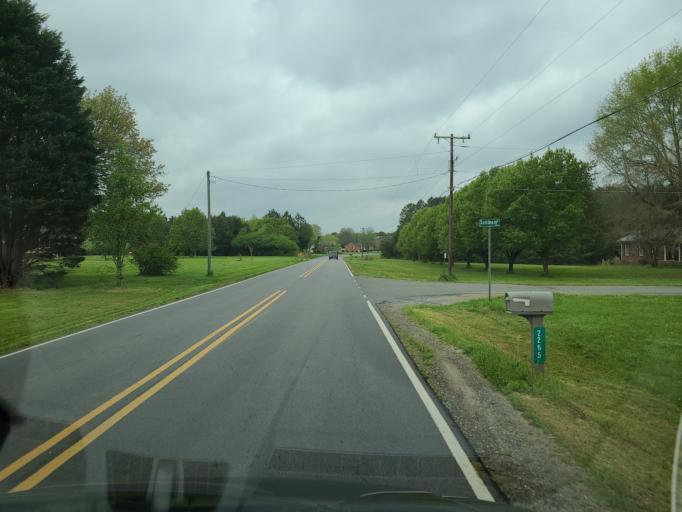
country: US
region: North Carolina
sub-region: Lincoln County
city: Lincolnton
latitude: 35.4569
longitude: -81.3111
